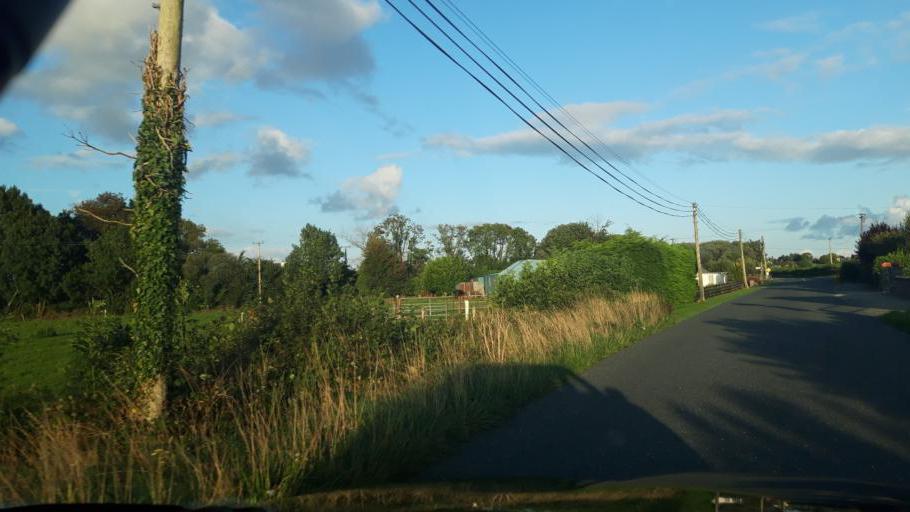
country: IE
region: Leinster
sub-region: An Iarmhi
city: Athlone
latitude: 53.4359
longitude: -7.8596
